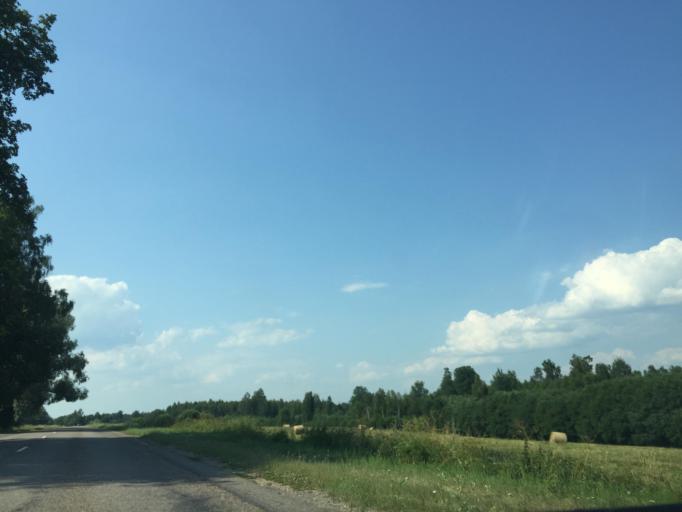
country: LV
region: Limbazu Rajons
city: Limbazi
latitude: 57.4785
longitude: 24.8754
